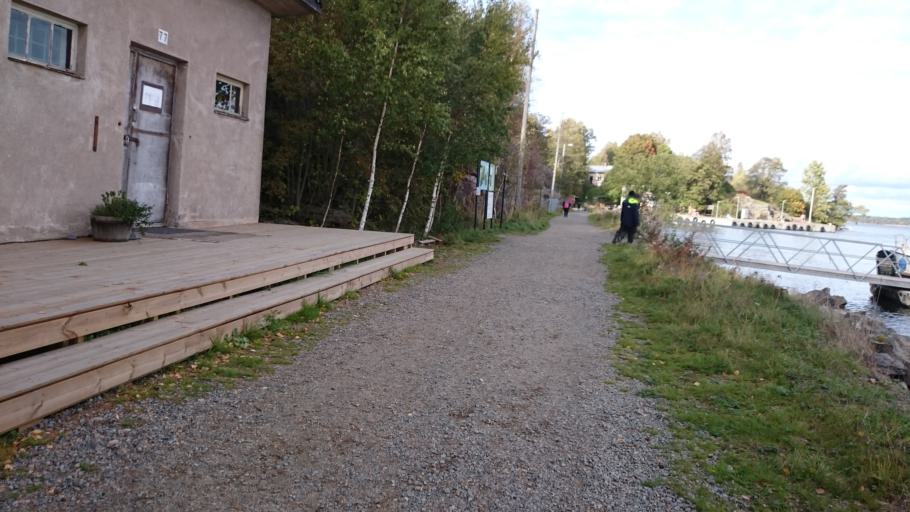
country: FI
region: Uusimaa
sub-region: Helsinki
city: Helsinki
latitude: 60.1362
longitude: 25.0097
